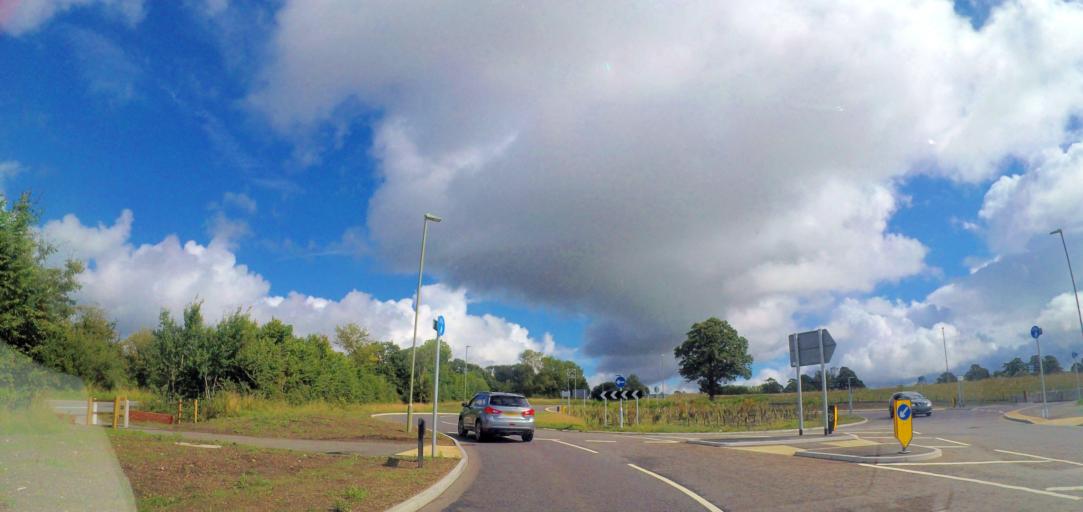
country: GB
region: England
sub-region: Hampshire
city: Bishopstoke
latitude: 50.9572
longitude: -1.3127
